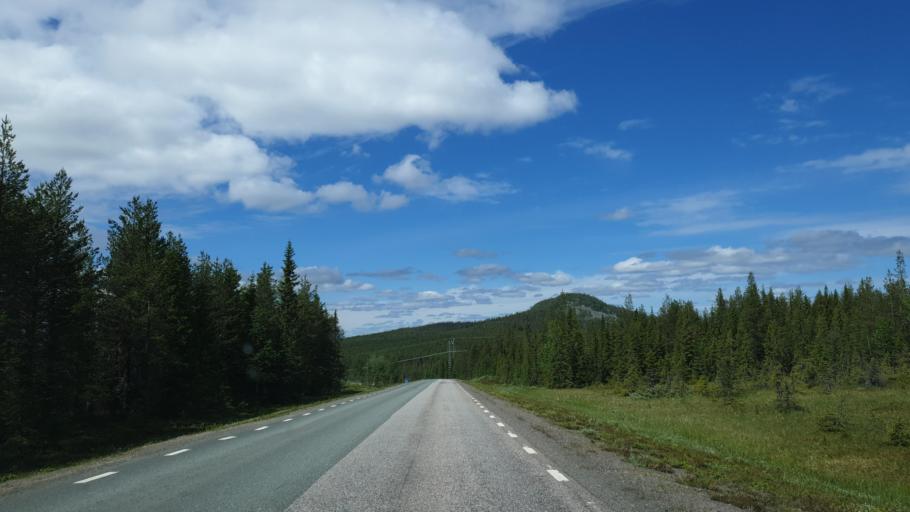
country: SE
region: Vaesterbotten
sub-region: Mala Kommun
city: Mala
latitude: 65.5723
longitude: 18.3474
